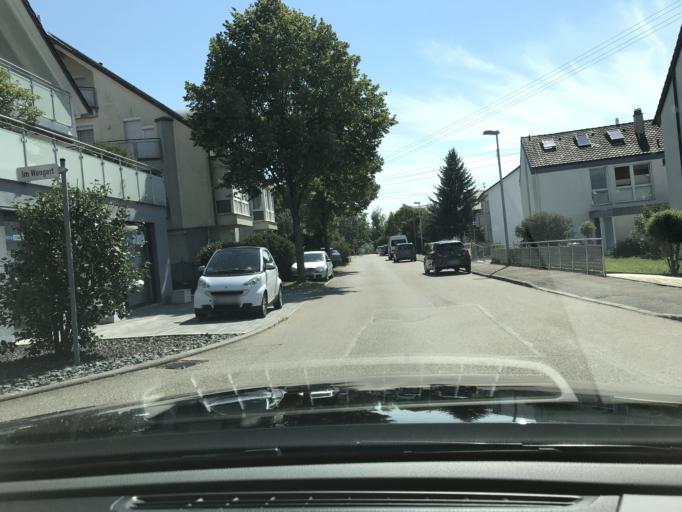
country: DE
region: Baden-Wuerttemberg
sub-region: Regierungsbezirk Stuttgart
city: Affalterbach
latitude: 48.8953
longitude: 9.3132
